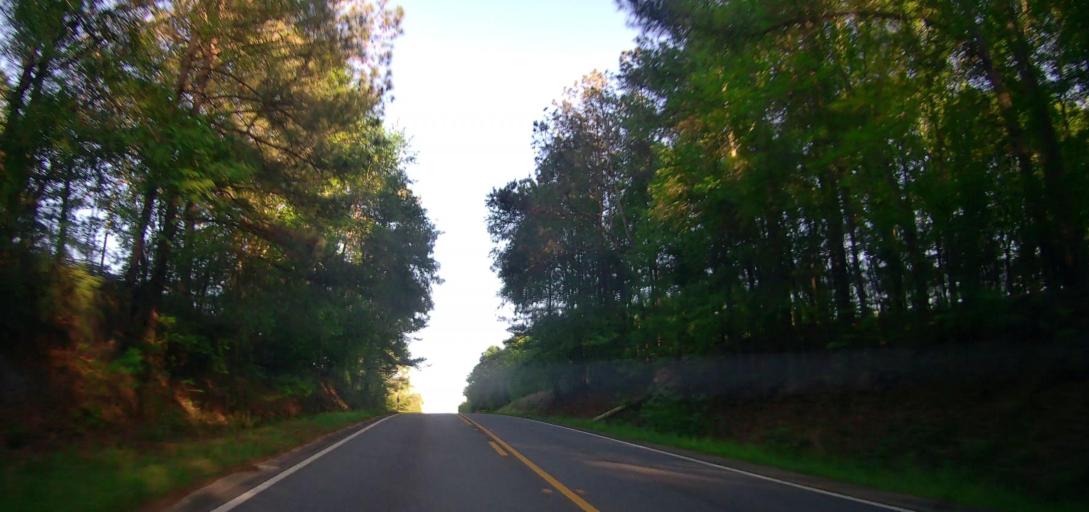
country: US
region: Georgia
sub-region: Marion County
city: Buena Vista
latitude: 32.3575
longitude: -84.3892
